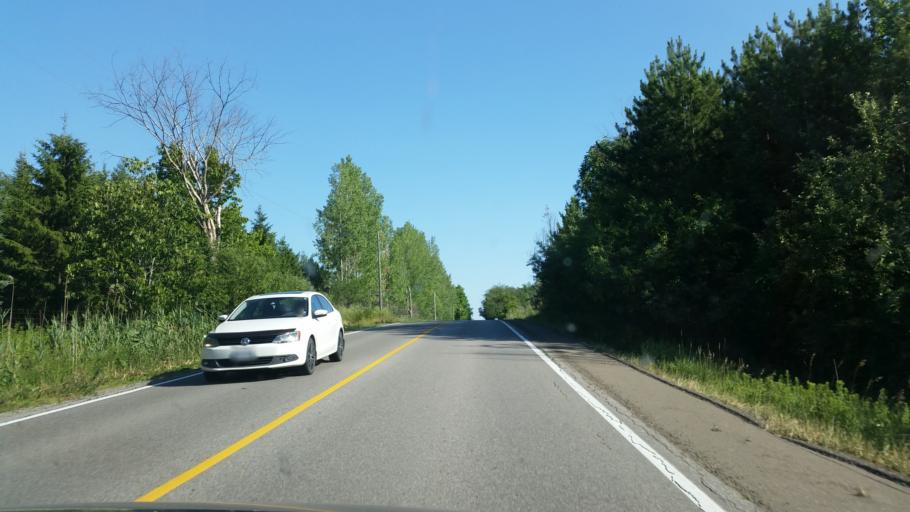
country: CA
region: Ontario
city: Bradford West Gwillimbury
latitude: 43.9337
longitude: -79.7438
